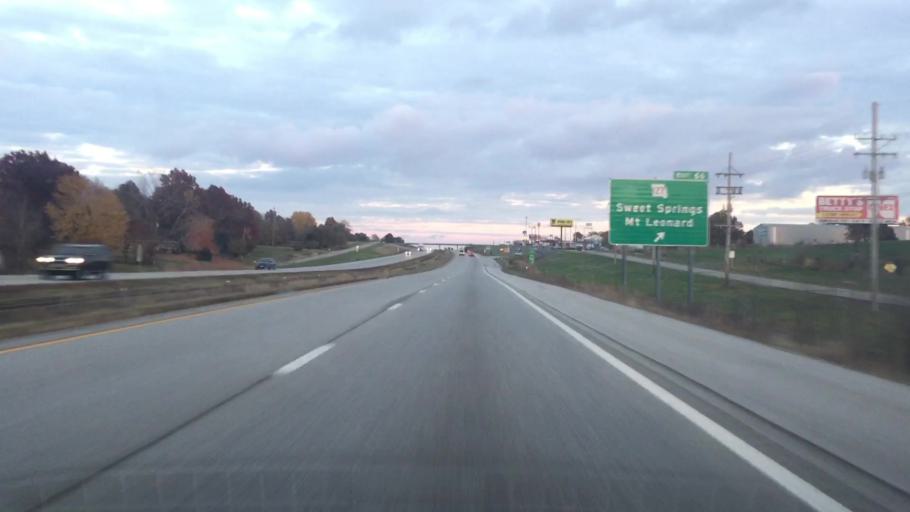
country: US
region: Missouri
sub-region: Saline County
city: Sweet Springs
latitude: 38.9772
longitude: -93.4253
